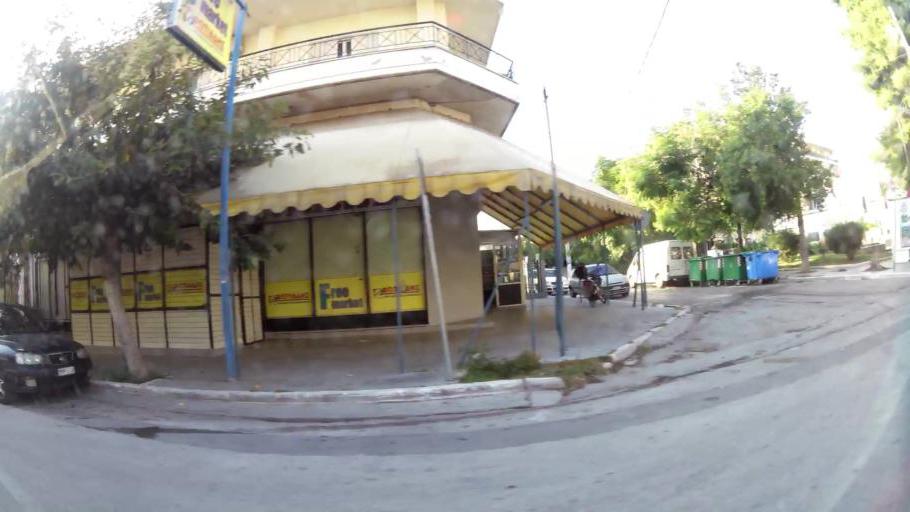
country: GR
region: Attica
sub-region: Nomarchia Anatolikis Attikis
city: Acharnes
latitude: 38.0861
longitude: 23.7405
